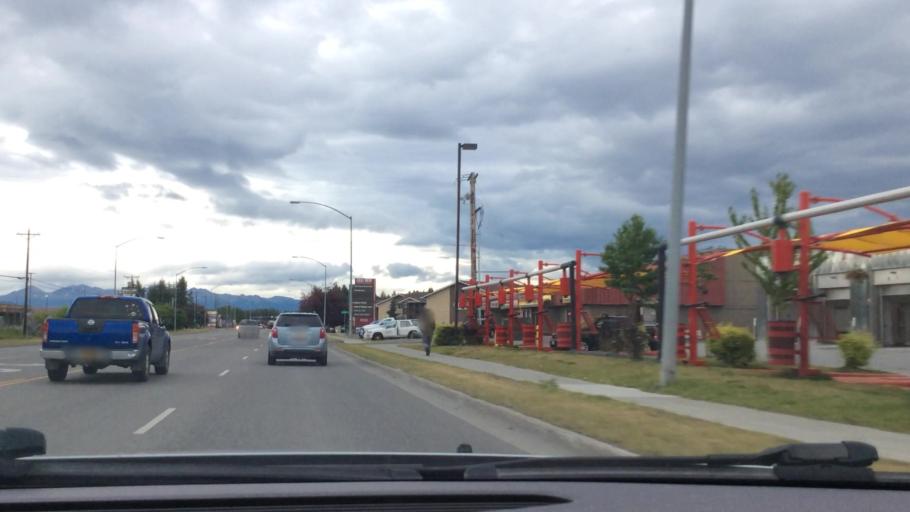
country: US
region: Alaska
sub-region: Anchorage Municipality
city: Anchorage
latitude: 61.1712
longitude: -149.8383
